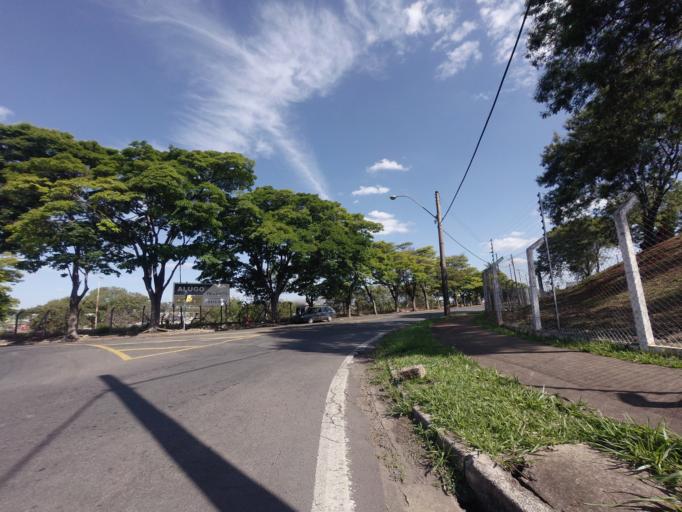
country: BR
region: Sao Paulo
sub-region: Piracicaba
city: Piracicaba
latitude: -22.7236
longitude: -47.5952
